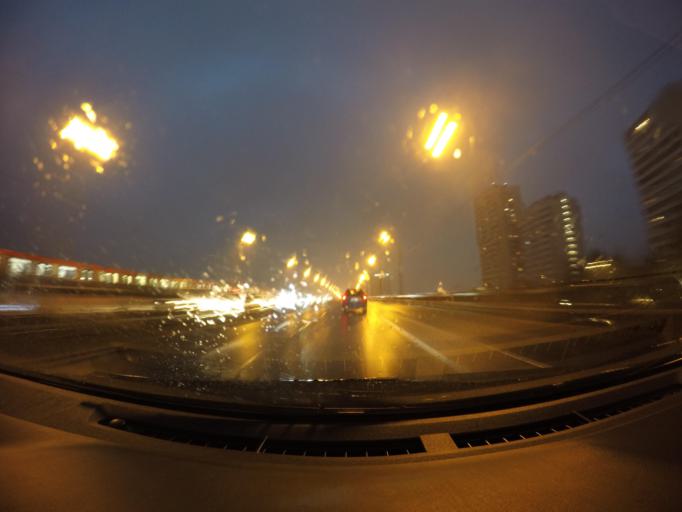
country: RU
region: Moskovskaya
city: Kozhukhovo
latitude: 55.6837
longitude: 37.6649
